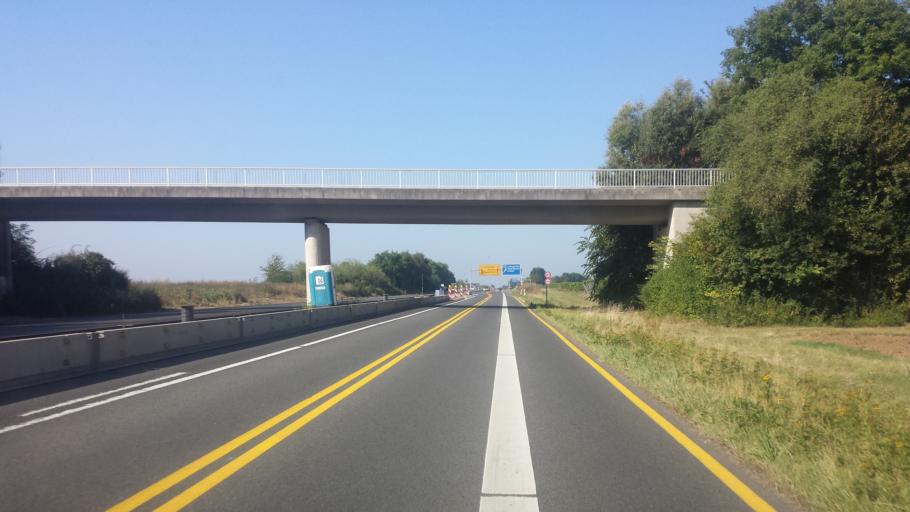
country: DE
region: Rheinland-Pfalz
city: Kleinniedesheim
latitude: 49.6241
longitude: 8.3073
